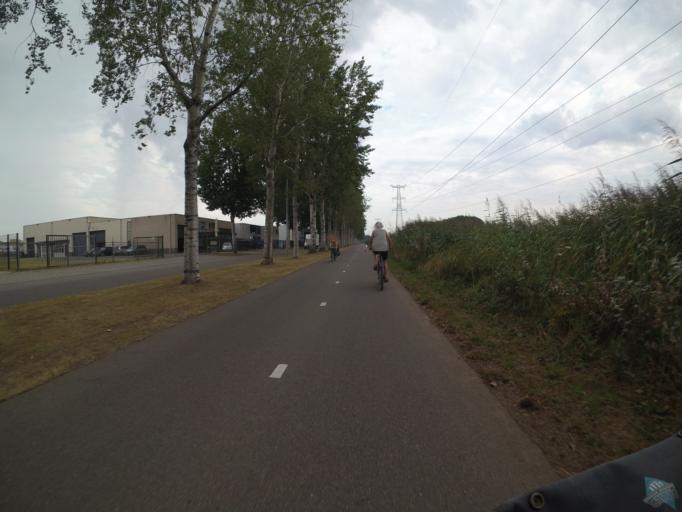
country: NL
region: North Brabant
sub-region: Gemeente Sint-Michielsgestel
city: Sint-Michielsgestel
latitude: 51.6860
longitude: 5.3641
